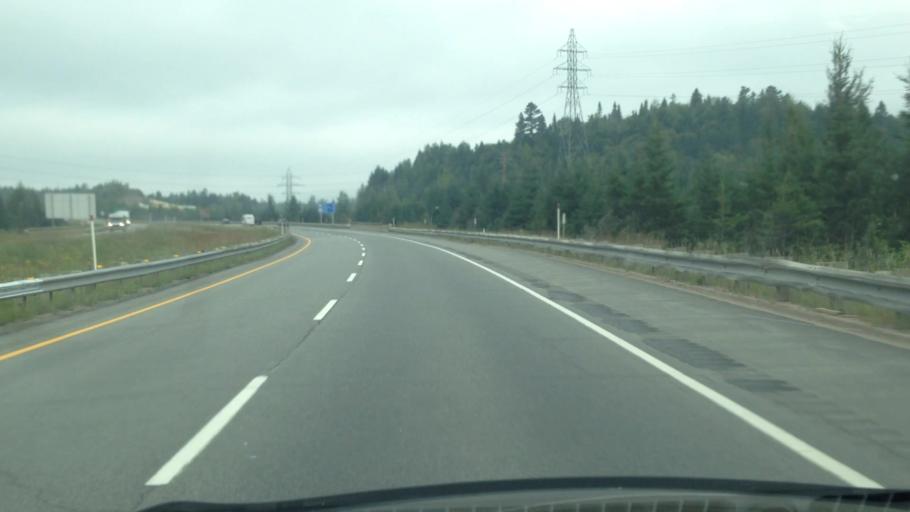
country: CA
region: Quebec
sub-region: Laurentides
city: Sainte-Agathe-des-Monts
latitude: 46.0602
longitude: -74.2763
